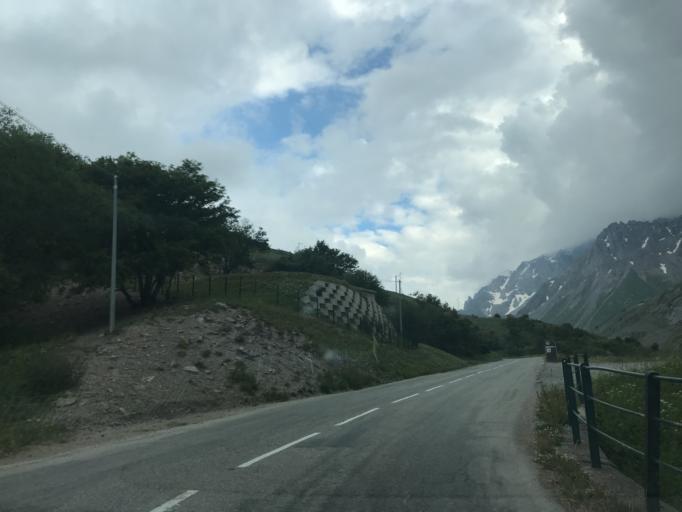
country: FR
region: Rhone-Alpes
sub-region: Departement de la Savoie
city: Valloire
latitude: 45.1042
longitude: 6.4273
